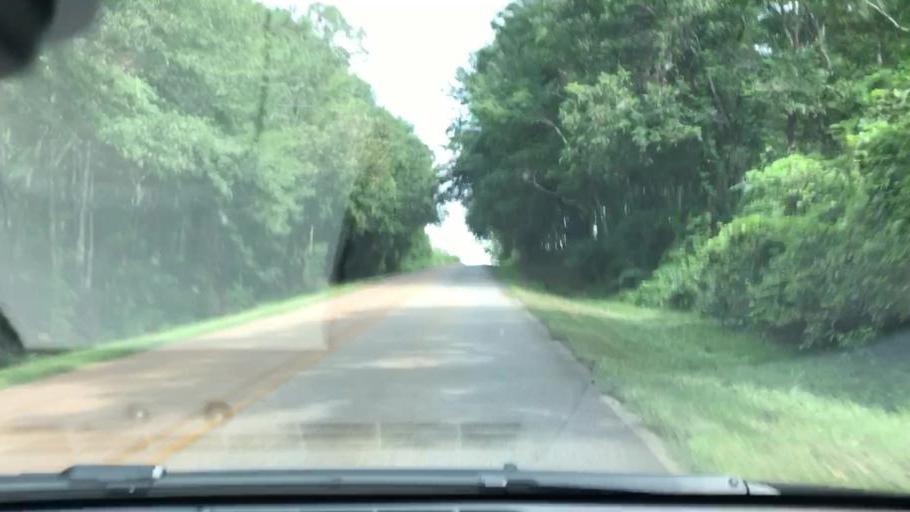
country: US
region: Georgia
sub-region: Clay County
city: Fort Gaines
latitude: 31.5697
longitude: -84.9974
